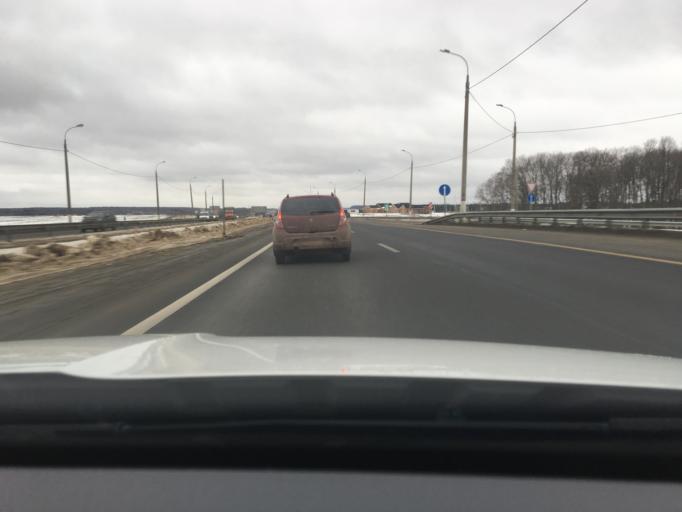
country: RU
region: Moskovskaya
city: Serpukhov
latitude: 54.8307
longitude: 37.4635
